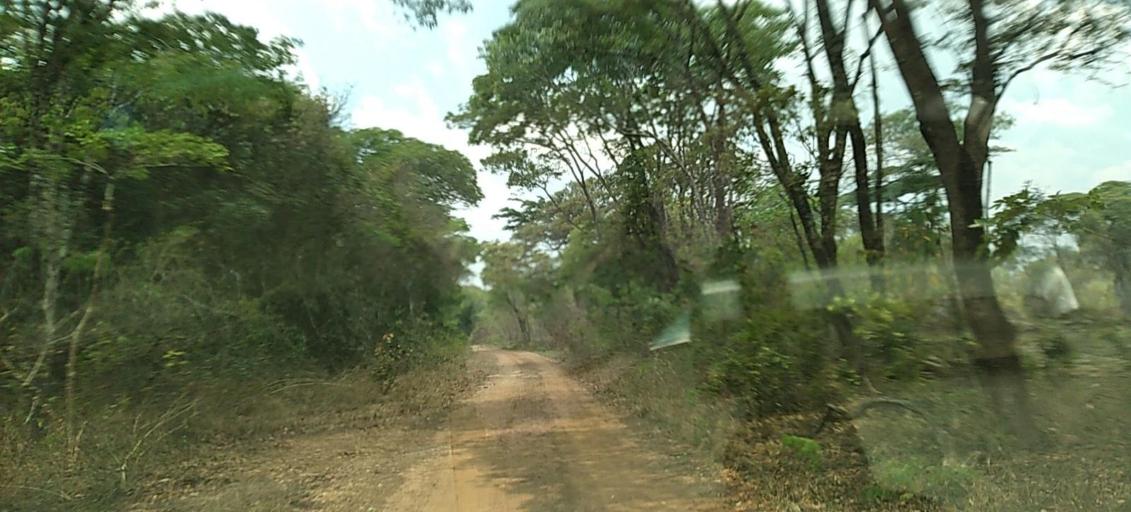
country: ZM
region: Copperbelt
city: Chingola
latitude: -12.7692
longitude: 27.7011
